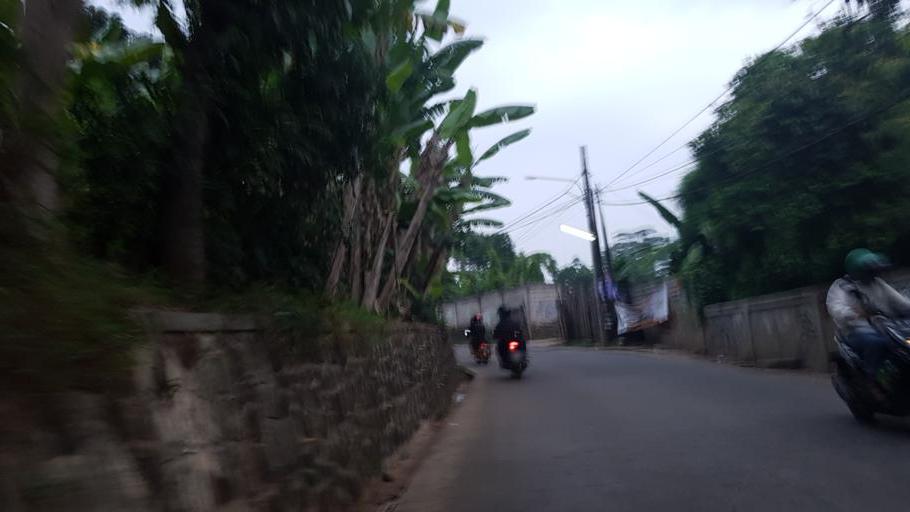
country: ID
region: West Java
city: Depok
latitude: -6.3664
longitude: 106.7947
